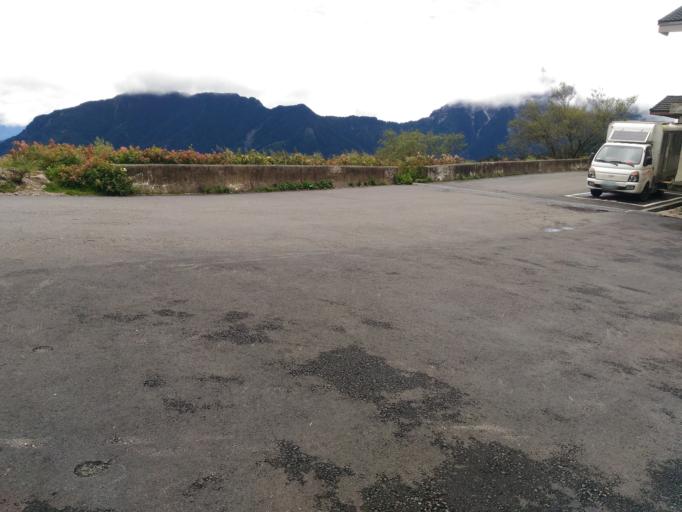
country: TW
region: Taiwan
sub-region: Hualien
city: Hualian
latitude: 24.1403
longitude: 121.2859
